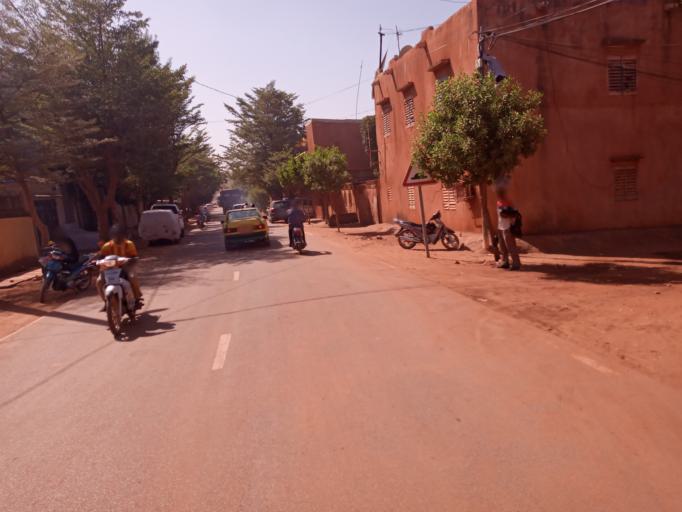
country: ML
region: Bamako
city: Bamako
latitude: 12.6134
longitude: -7.9551
